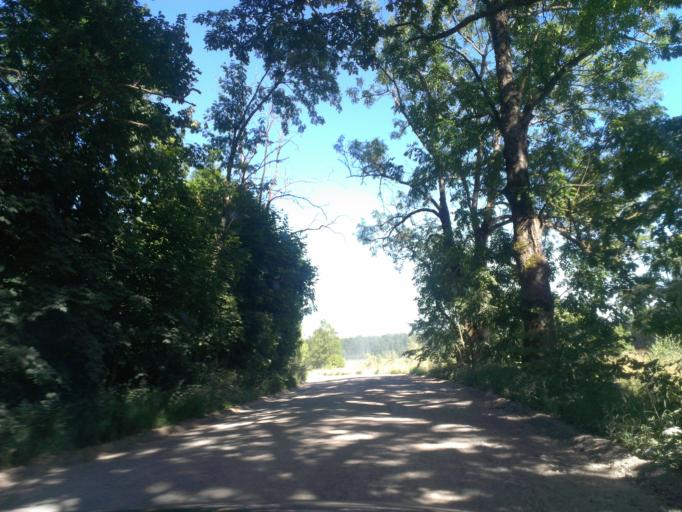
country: LV
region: Malpils
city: Malpils
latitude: 57.0591
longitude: 25.1649
